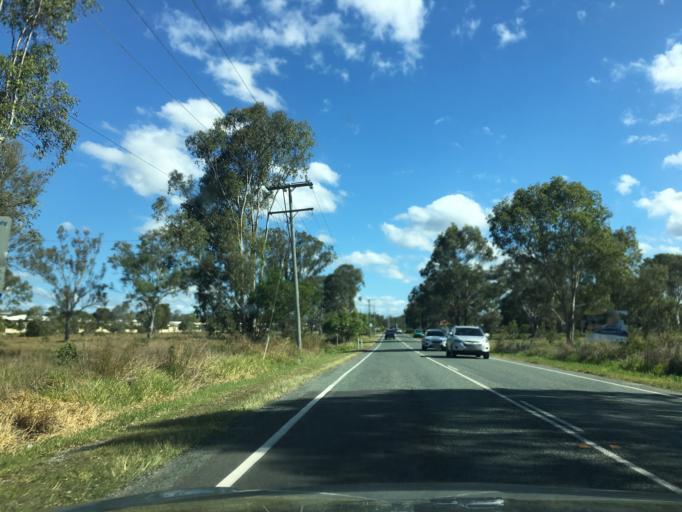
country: AU
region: Queensland
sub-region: Logan
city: Chambers Flat
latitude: -27.7627
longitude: 153.1099
